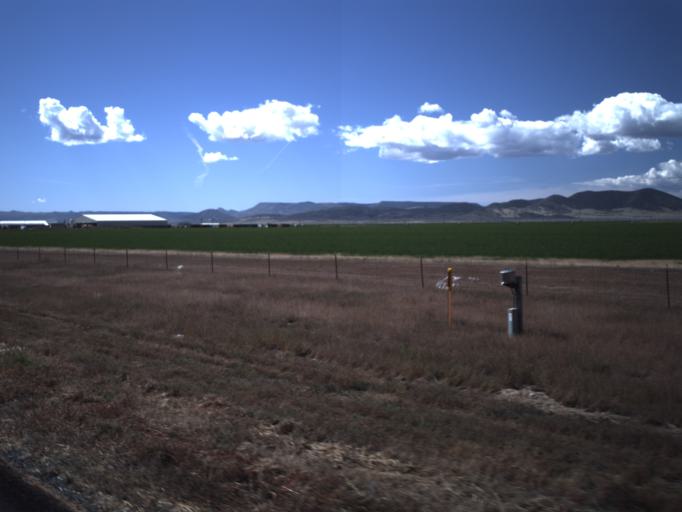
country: US
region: Utah
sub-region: Washington County
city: Enterprise
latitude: 37.6845
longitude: -113.6565
